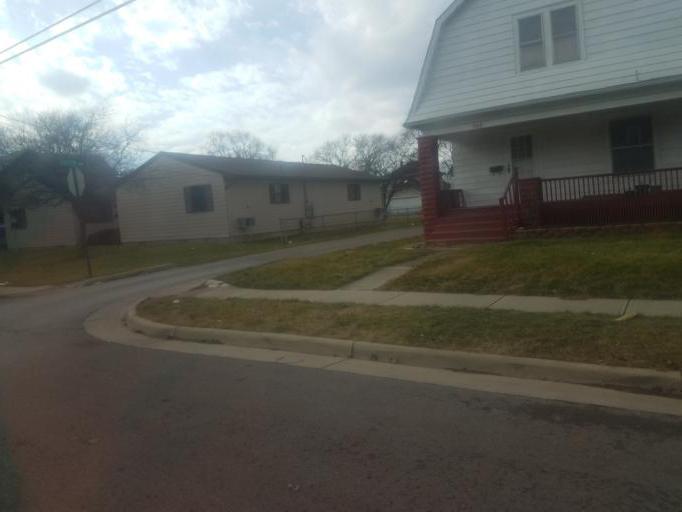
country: US
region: Ohio
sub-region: Marion County
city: Marion
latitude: 40.5807
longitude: -83.1366
